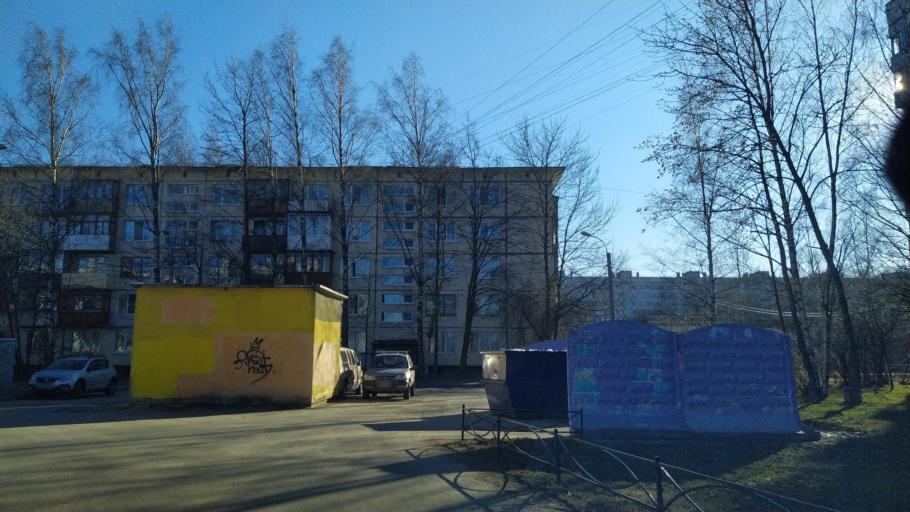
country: RU
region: St.-Petersburg
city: Grazhdanka
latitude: 60.0471
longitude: 30.4015
